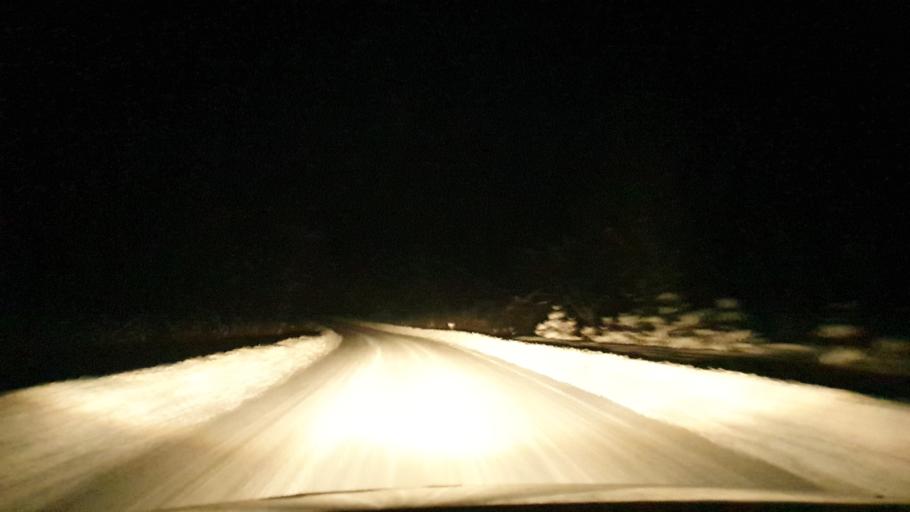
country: EE
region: Vorumaa
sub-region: Antsla vald
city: Vana-Antsla
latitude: 57.9635
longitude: 26.6428
